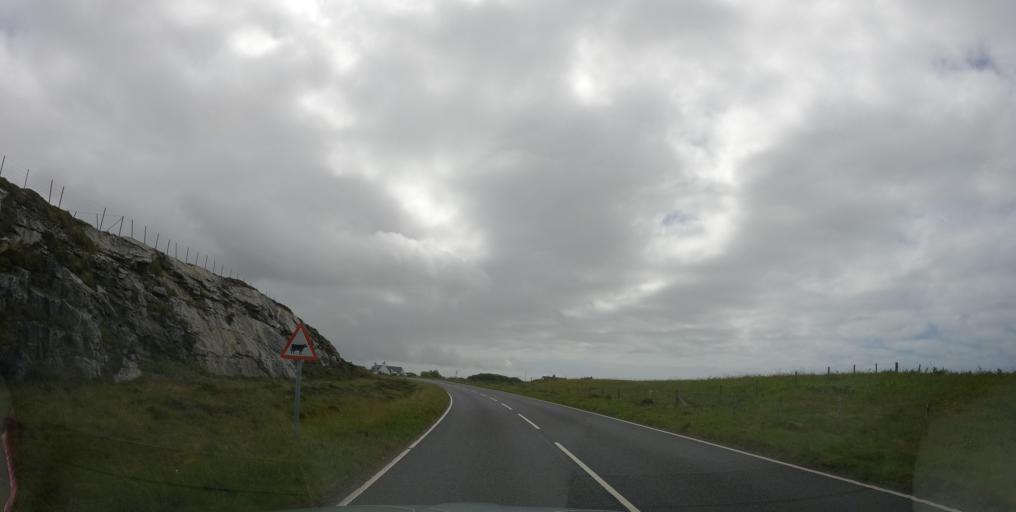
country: GB
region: Scotland
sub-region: Eilean Siar
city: Isle of South Uist
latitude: 57.3032
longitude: -7.3724
